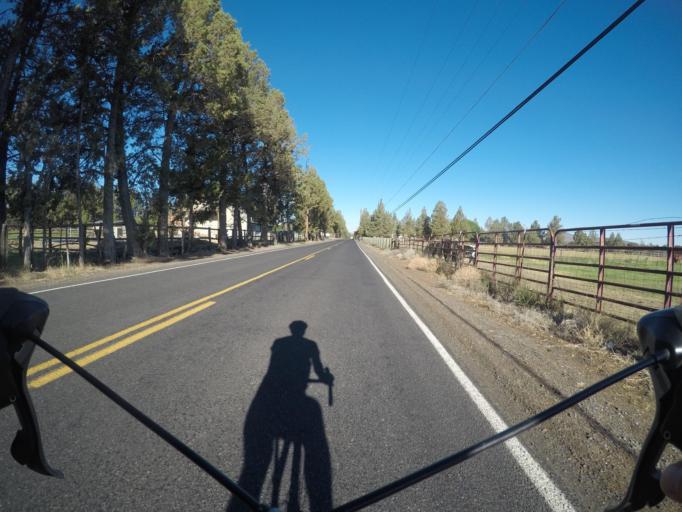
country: US
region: Oregon
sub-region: Deschutes County
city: Redmond
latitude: 44.2186
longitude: -121.2421
